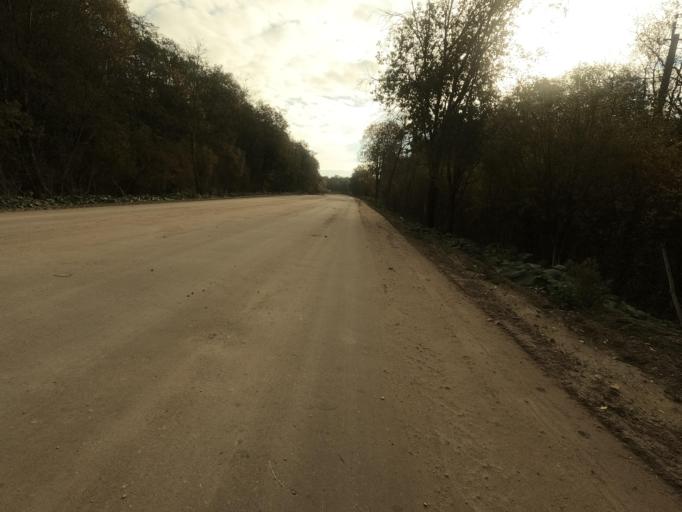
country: RU
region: Novgorod
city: Batetskiy
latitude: 58.7993
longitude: 30.6334
